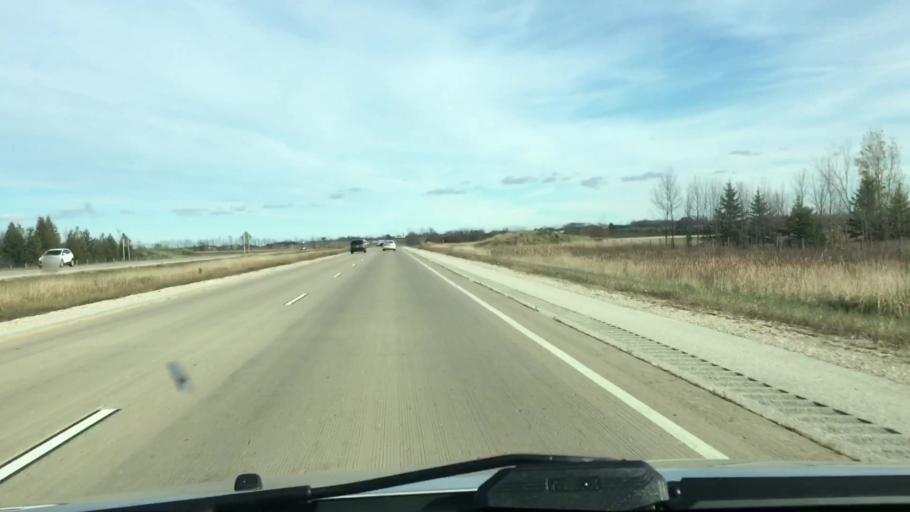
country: US
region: Wisconsin
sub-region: Kewaunee County
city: Luxemburg
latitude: 44.7163
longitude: -87.6439
